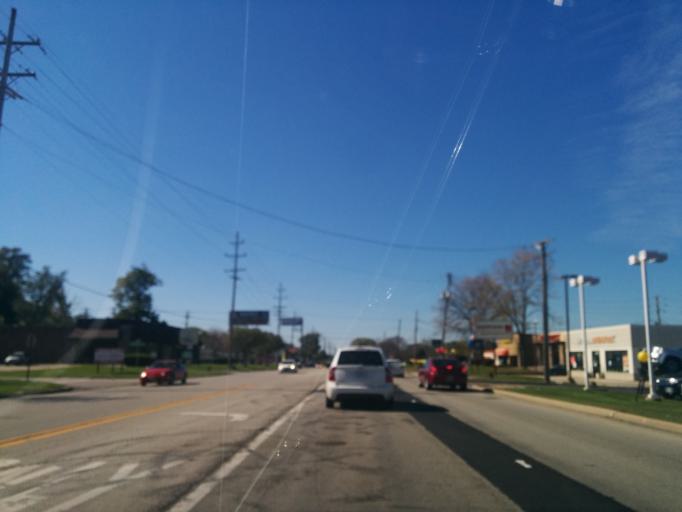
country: US
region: Illinois
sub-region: DuPage County
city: Oakbrook Terrace
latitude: 41.8605
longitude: -87.9860
